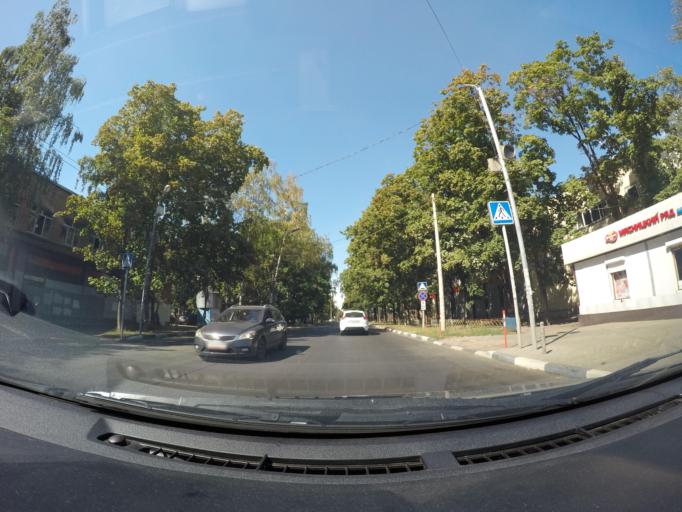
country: RU
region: Moskovskaya
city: Tomilino
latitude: 55.6679
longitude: 37.9227
